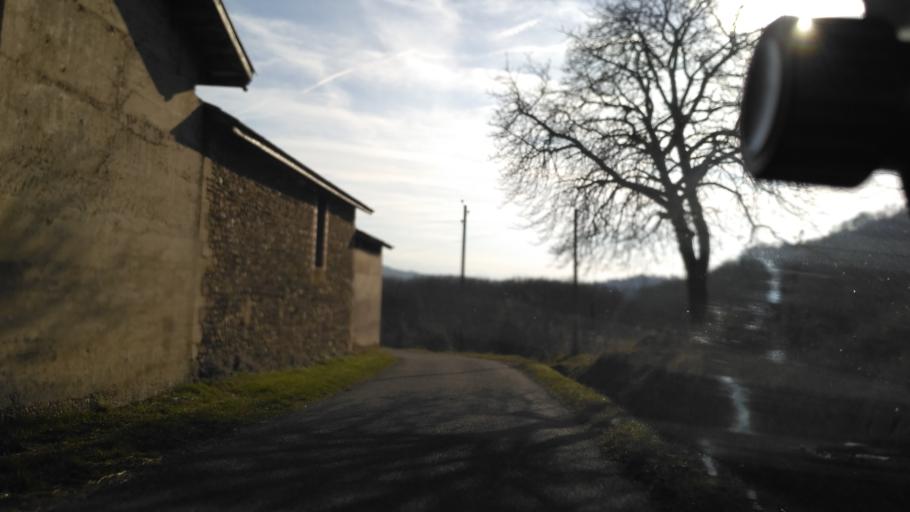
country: FR
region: Rhone-Alpes
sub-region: Departement de l'Isere
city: Saint-Lattier
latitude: 45.1309
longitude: 5.1518
